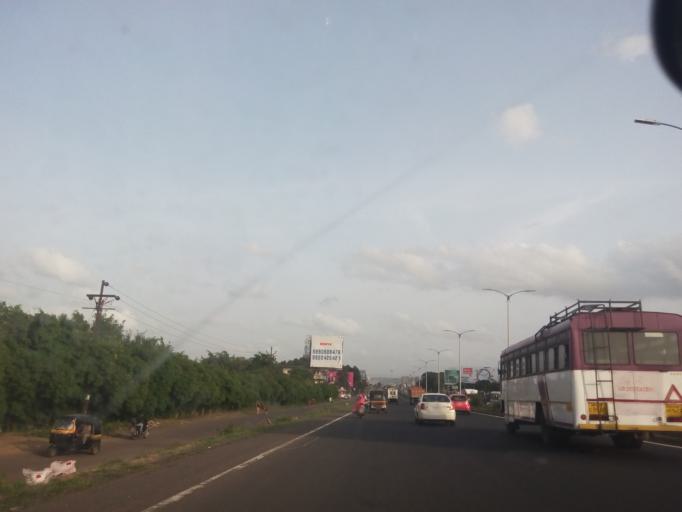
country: IN
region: Maharashtra
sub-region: Pune Division
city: Pimpri
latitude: 18.6145
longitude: 73.7489
